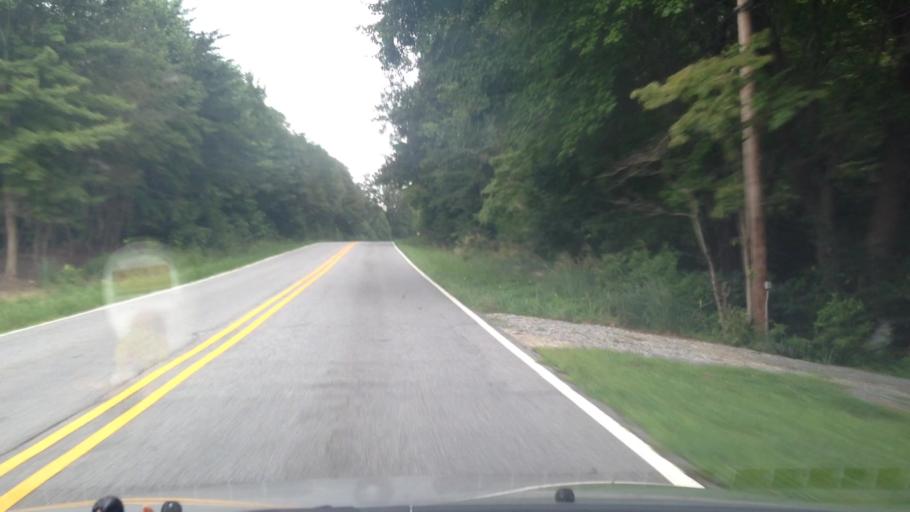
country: US
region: North Carolina
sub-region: Forsyth County
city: Walkertown
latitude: 36.2038
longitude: -80.1677
